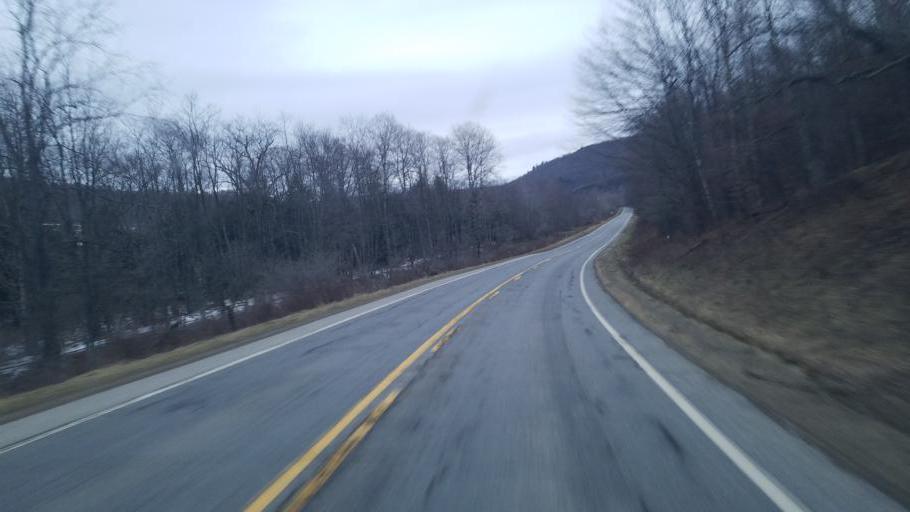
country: US
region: Pennsylvania
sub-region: Potter County
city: Coudersport
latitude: 41.8325
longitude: -77.9098
